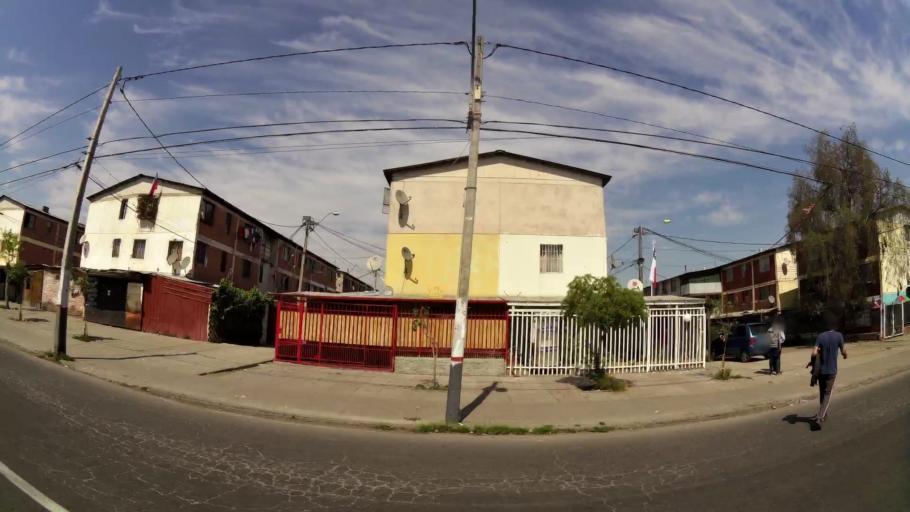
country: CL
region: Santiago Metropolitan
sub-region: Provincia de Santiago
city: La Pintana
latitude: -33.5577
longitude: -70.6355
